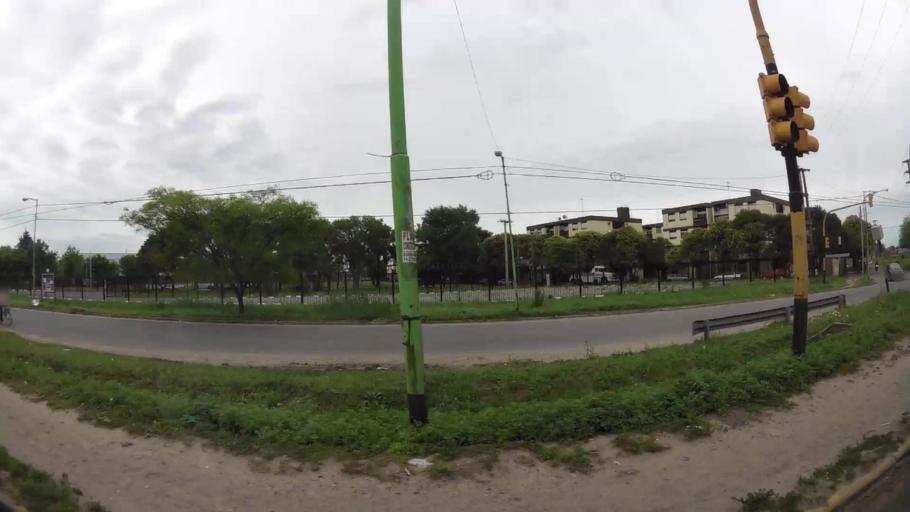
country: AR
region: Buenos Aires
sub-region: Partido de Campana
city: Campana
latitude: -34.1858
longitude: -58.9433
